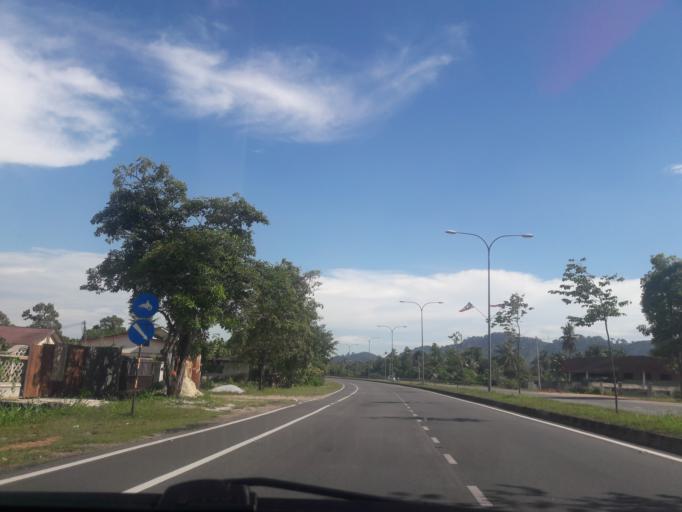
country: MY
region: Kedah
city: Sungai Petani
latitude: 5.6254
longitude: 100.4638
